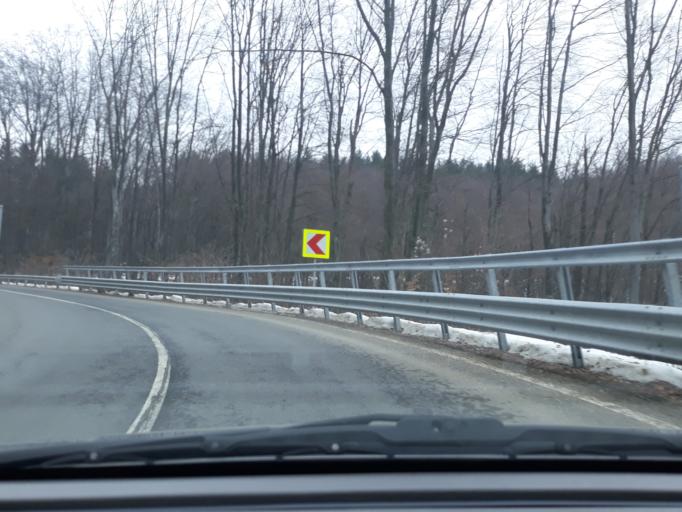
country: RO
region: Bihor
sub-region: Oras Alesd
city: Padurea Neagra
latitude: 47.1270
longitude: 22.4236
